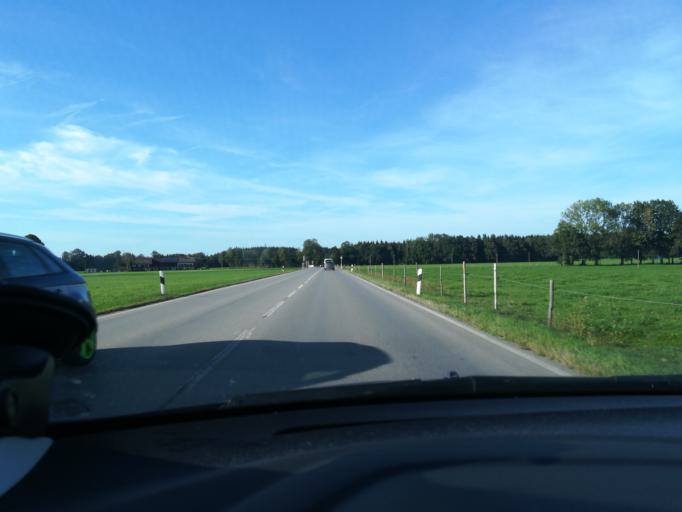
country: DE
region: Bavaria
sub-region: Upper Bavaria
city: Miesbach
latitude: 47.8038
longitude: 11.8381
